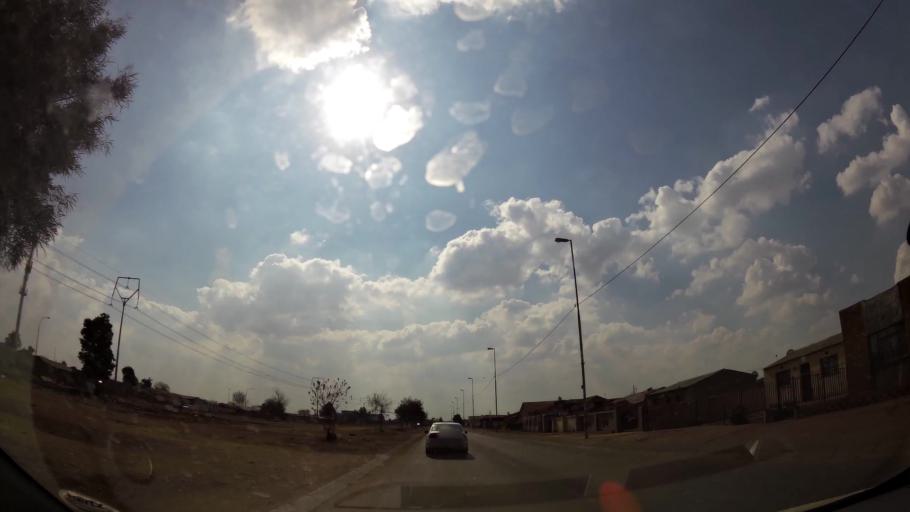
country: ZA
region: Gauteng
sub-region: Ekurhuleni Metropolitan Municipality
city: Germiston
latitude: -26.3366
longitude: 28.1439
